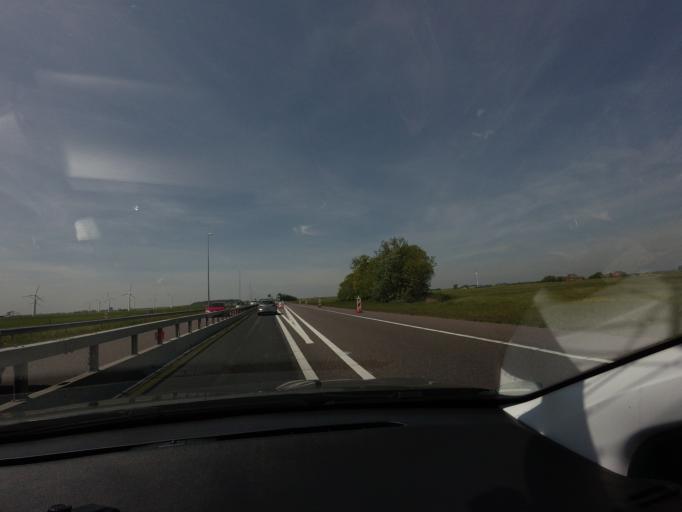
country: NL
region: Friesland
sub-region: Sudwest Fryslan
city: Makkum
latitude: 53.0954
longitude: 5.4089
